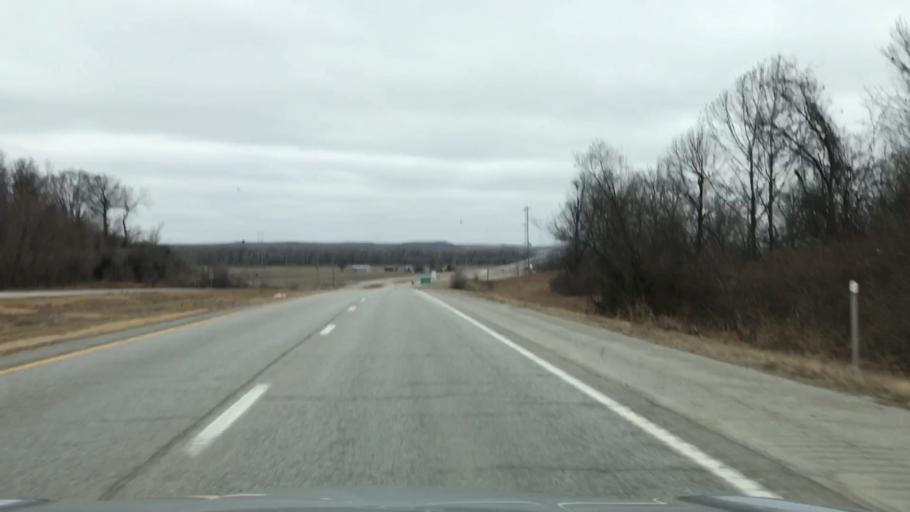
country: US
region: Missouri
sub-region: Jackson County
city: Independence
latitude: 39.1527
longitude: -94.3933
